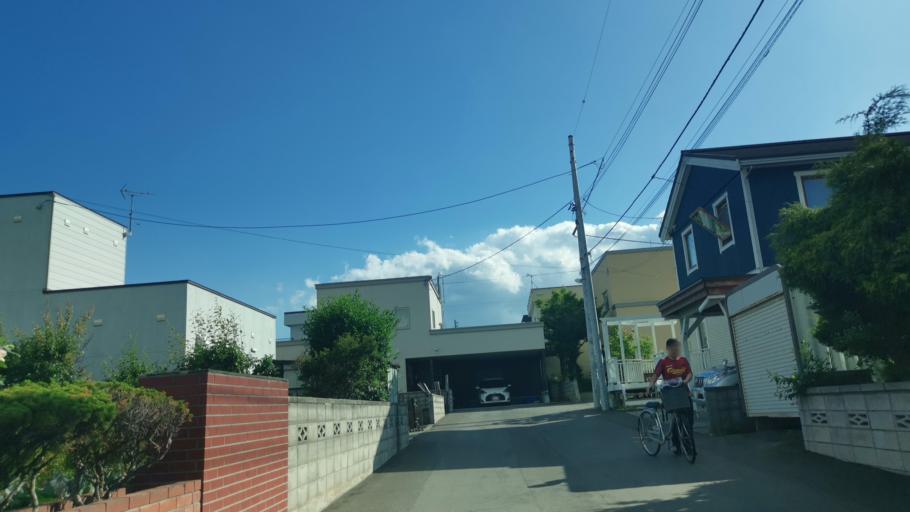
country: JP
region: Hokkaido
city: Sapporo
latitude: 43.0758
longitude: 141.2748
